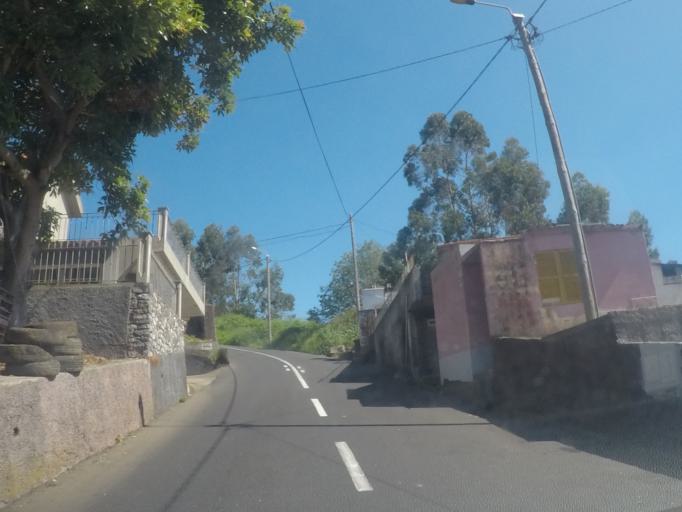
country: PT
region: Madeira
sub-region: Camara de Lobos
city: Curral das Freiras
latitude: 32.6808
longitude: -16.9672
